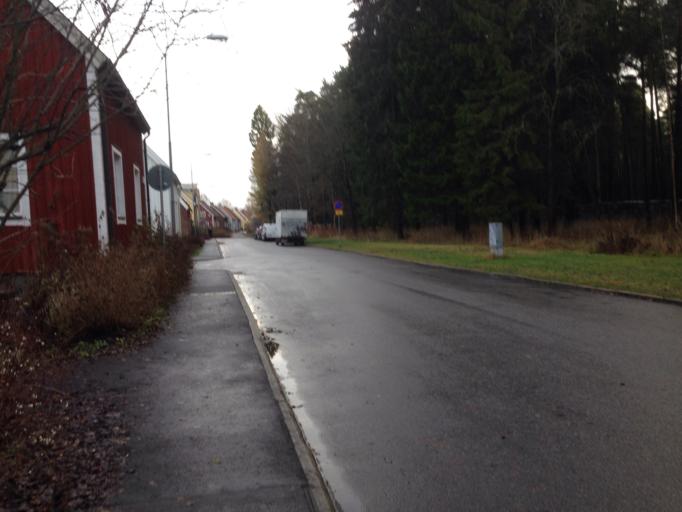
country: SE
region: Stockholm
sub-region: Stockholms Kommun
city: Arsta
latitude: 59.2790
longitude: 18.1020
